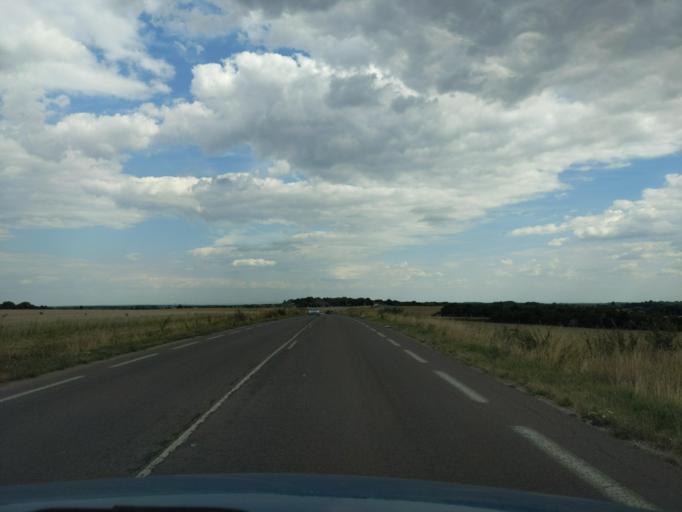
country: FR
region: Bourgogne
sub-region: Departement de la Cote-d'Or
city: Sennecey-les-Dijon
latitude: 47.2945
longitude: 5.0863
